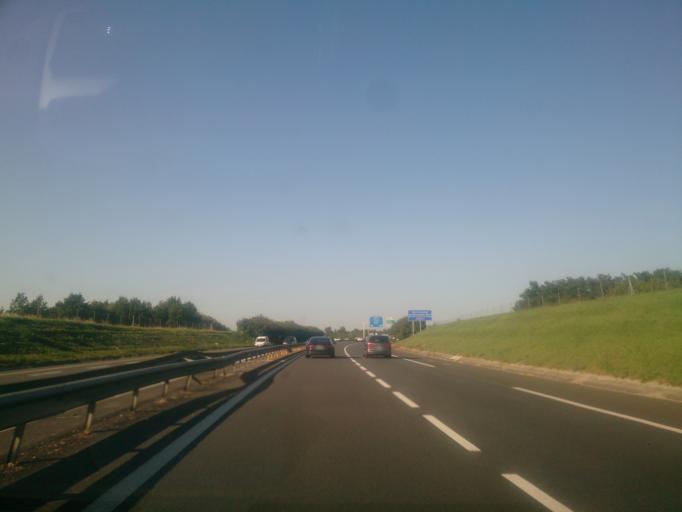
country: FR
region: Midi-Pyrenees
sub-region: Departement du Tarn-et-Garonne
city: Montauban
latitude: 44.0414
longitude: 1.3896
